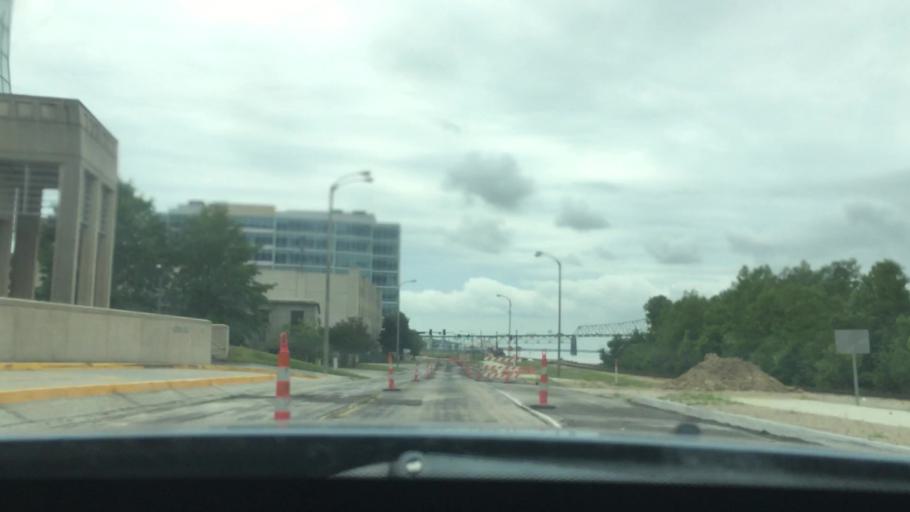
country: US
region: Louisiana
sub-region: West Baton Rouge Parish
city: Port Allen
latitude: 30.4544
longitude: -91.1902
